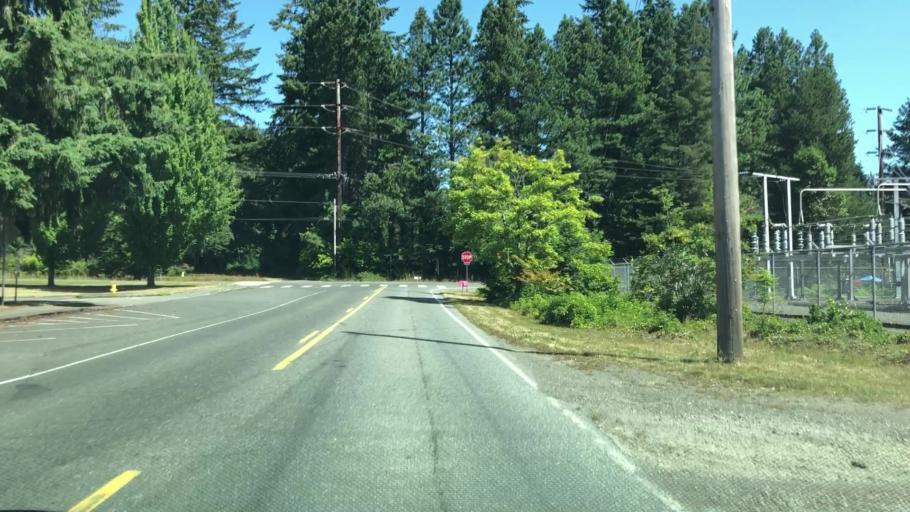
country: US
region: Washington
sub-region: Snohomish County
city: Maltby
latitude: 47.7681
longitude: -122.1157
